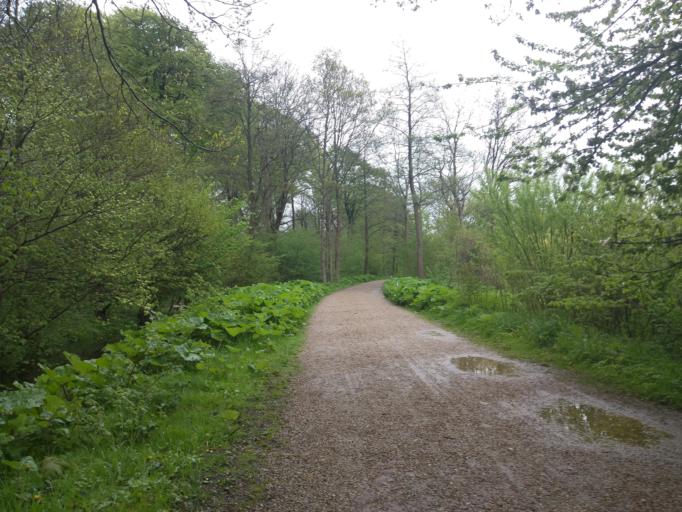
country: DK
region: Central Jutland
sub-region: Viborg Kommune
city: Viborg
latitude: 56.4457
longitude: 9.4217
